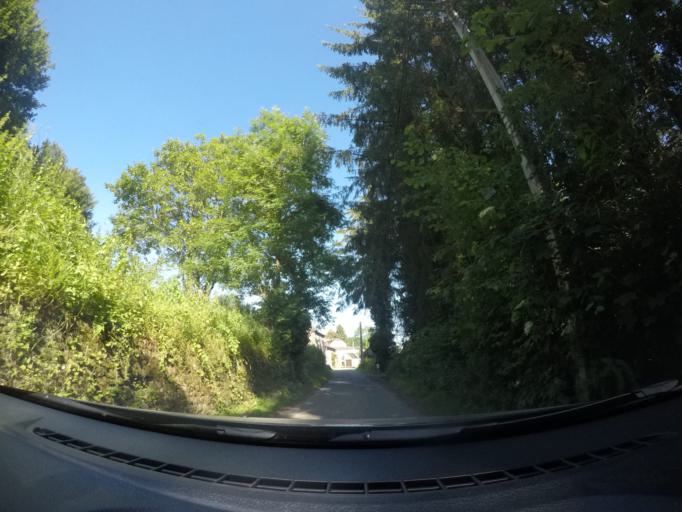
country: BE
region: Wallonia
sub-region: Province de Namur
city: Philippeville
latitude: 50.1683
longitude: 4.5581
